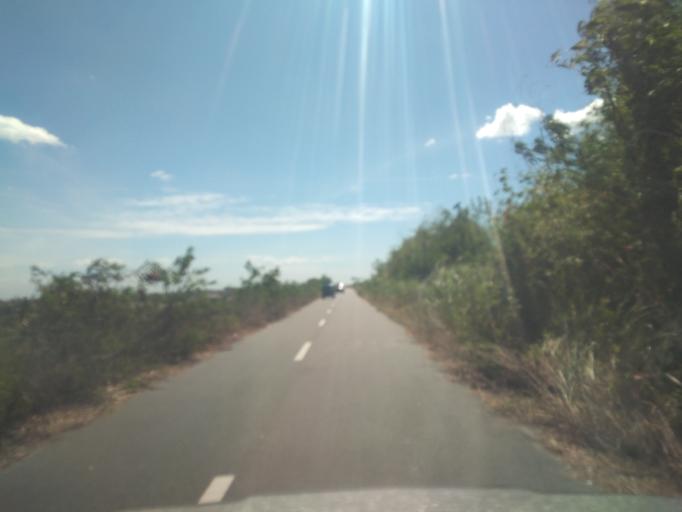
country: PH
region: Central Luzon
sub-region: Province of Pampanga
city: San Basilio
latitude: 15.0256
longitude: 120.6000
